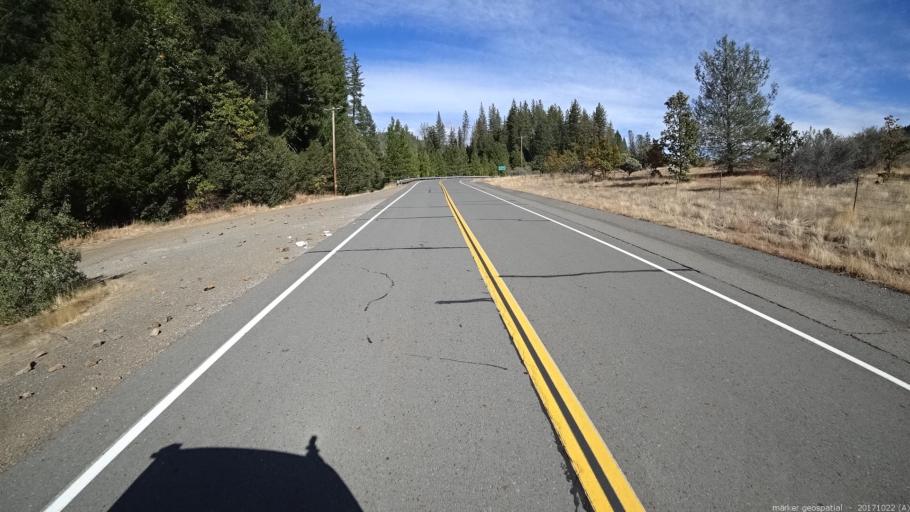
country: US
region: California
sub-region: Siskiyou County
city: Dunsmuir
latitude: 40.9773
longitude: -122.4340
